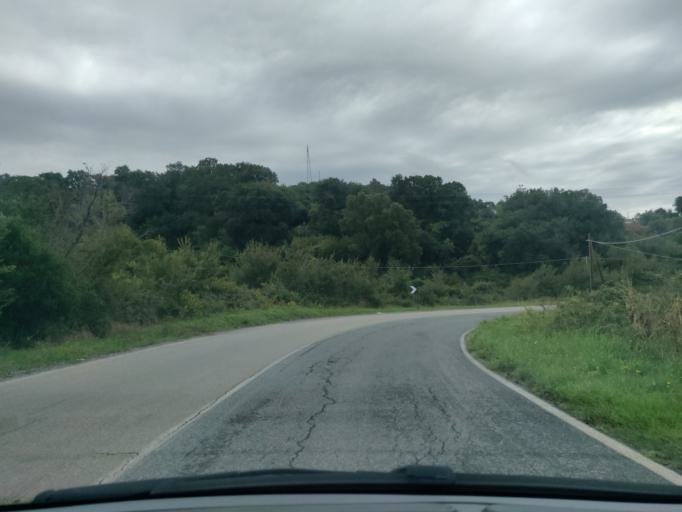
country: IT
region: Latium
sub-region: Citta metropolitana di Roma Capitale
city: Civitavecchia
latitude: 42.1103
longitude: 11.8438
